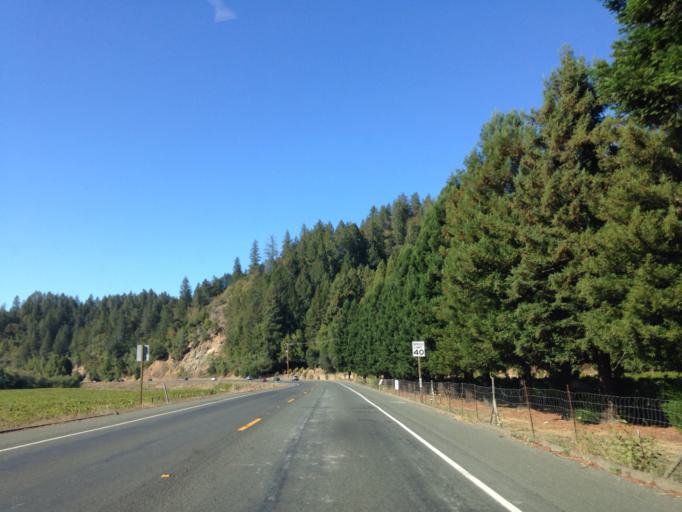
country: US
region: California
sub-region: Sonoma County
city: Guerneville
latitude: 38.5145
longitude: -122.9674
